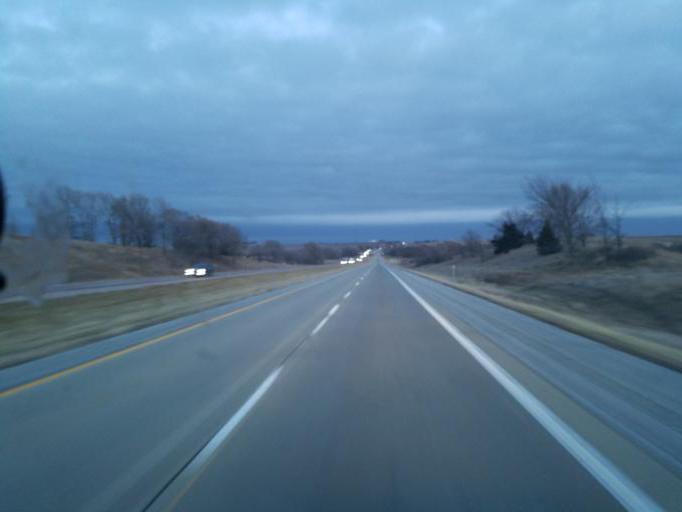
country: US
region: Iowa
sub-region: Cass County
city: Atlantic
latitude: 41.4981
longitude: -95.1530
